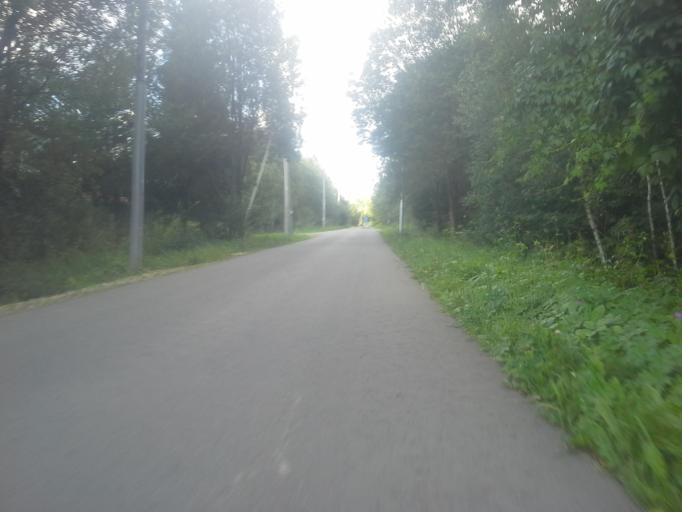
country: RU
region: Moskovskaya
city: Kievskij
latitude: 55.3480
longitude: 36.9458
